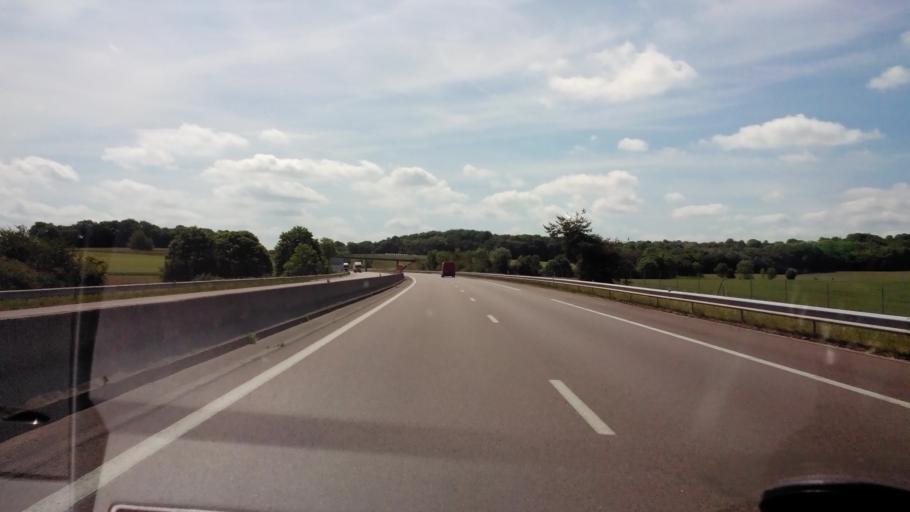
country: FR
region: Lorraine
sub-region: Departement des Vosges
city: Chatenois
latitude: 48.4145
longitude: 5.8646
